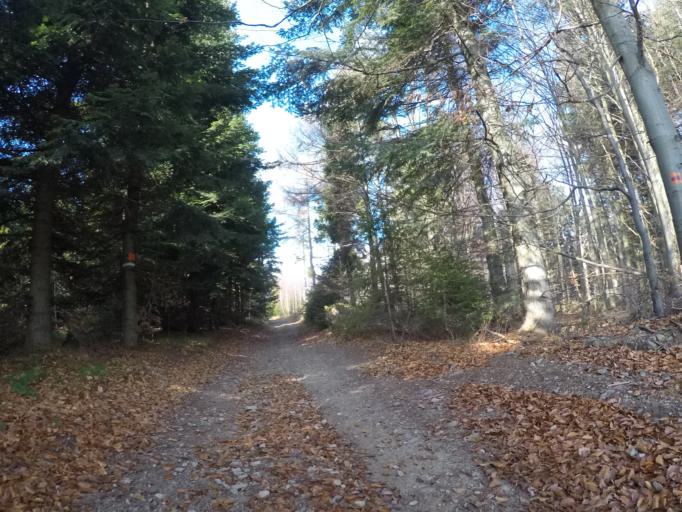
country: SK
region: Kosicky
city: Gelnica
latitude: 48.7648
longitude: 21.0638
